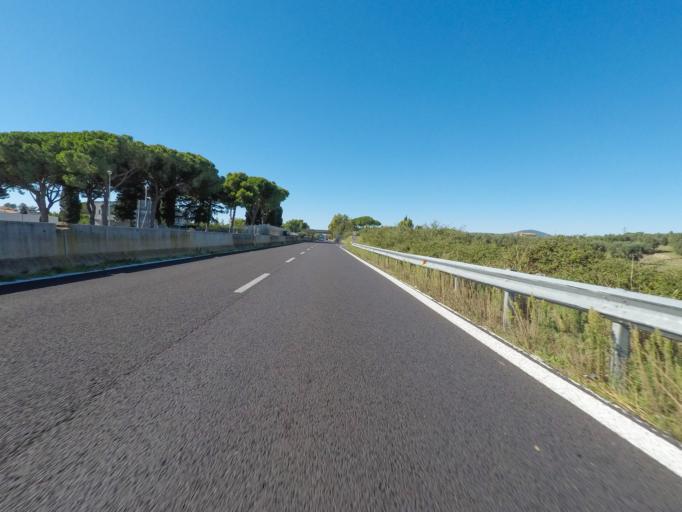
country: IT
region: Latium
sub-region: Provincia di Viterbo
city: Pescia Romana
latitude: 42.4017
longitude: 11.5020
